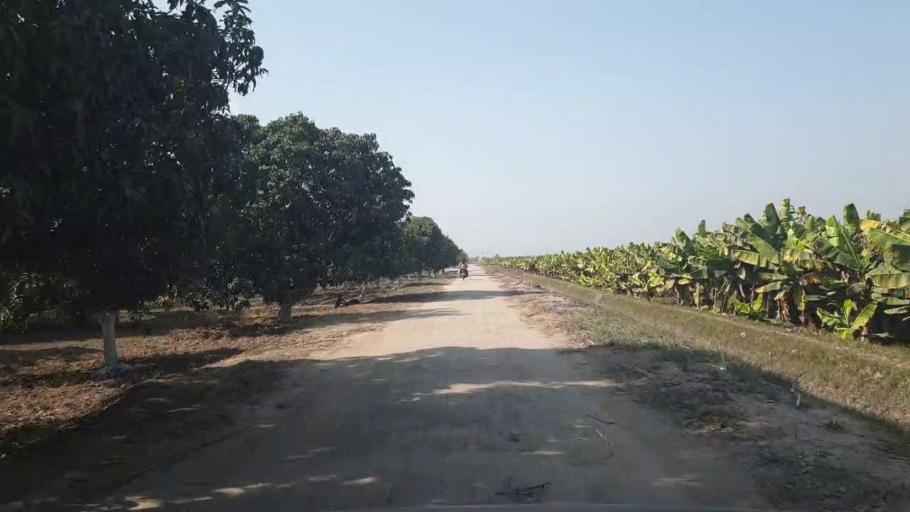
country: PK
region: Sindh
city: Tando Adam
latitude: 25.7694
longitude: 68.5986
